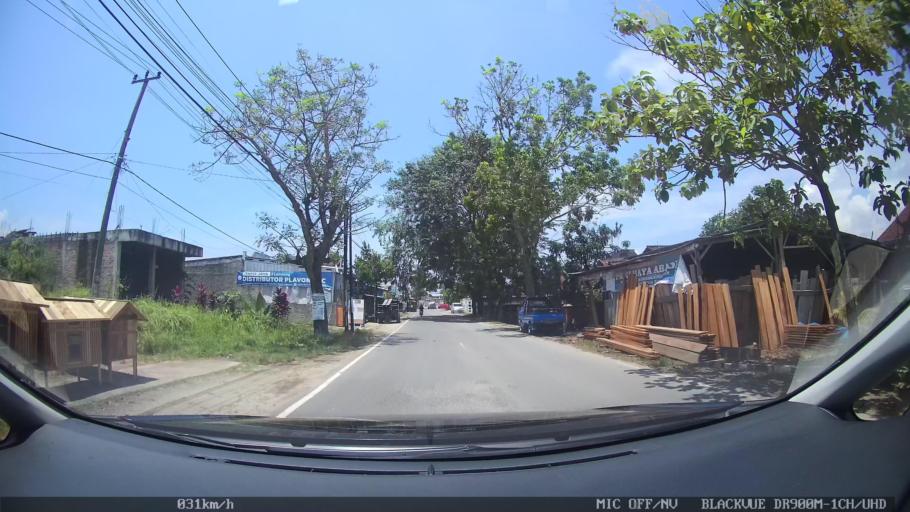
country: ID
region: Lampung
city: Kedaton
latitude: -5.3713
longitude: 105.2894
